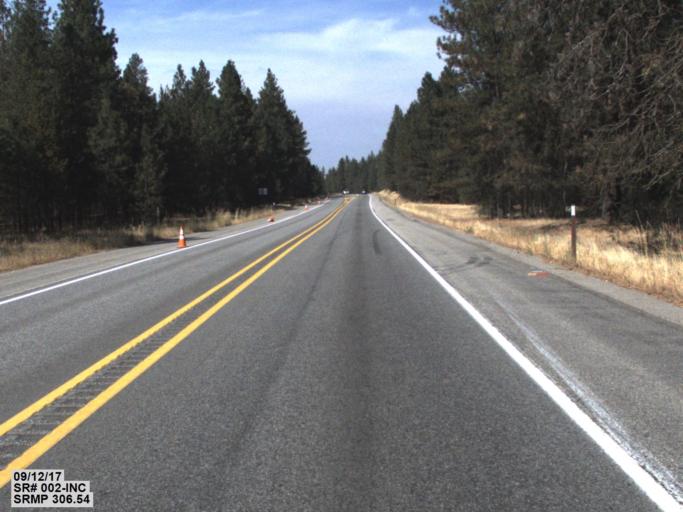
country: US
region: Washington
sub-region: Spokane County
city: Deer Park
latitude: 47.9190
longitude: -117.3501
